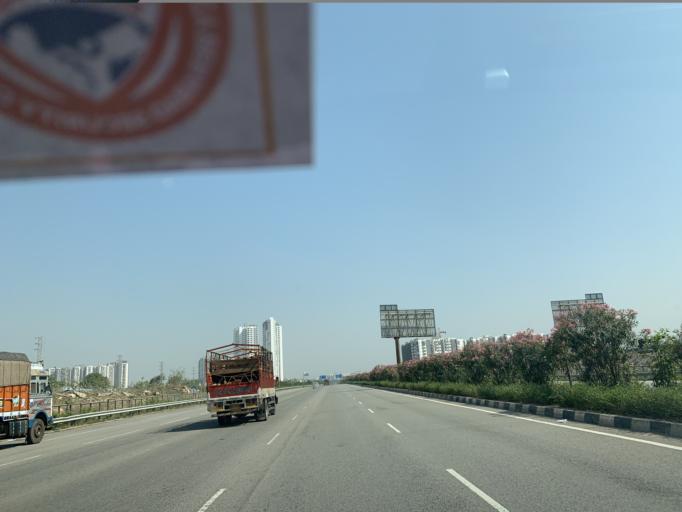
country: IN
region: Telangana
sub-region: Medak
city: Serilingampalle
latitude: 17.4034
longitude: 78.3380
